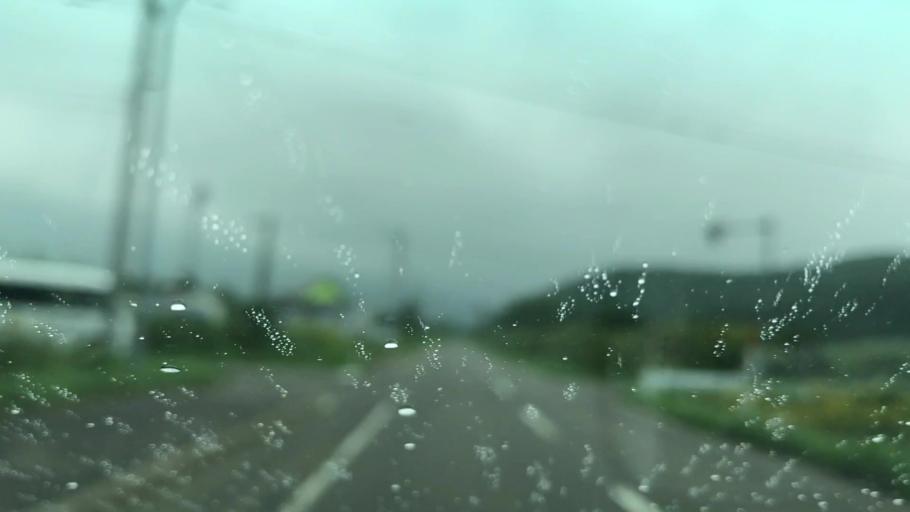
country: JP
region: Hokkaido
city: Iwanai
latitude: 42.7486
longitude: 140.2844
